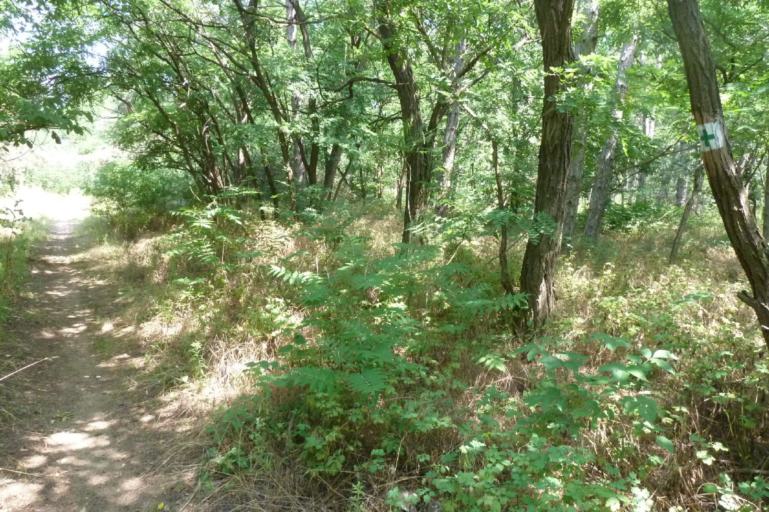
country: HU
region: Pest
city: Fot
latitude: 47.6368
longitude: 19.2140
